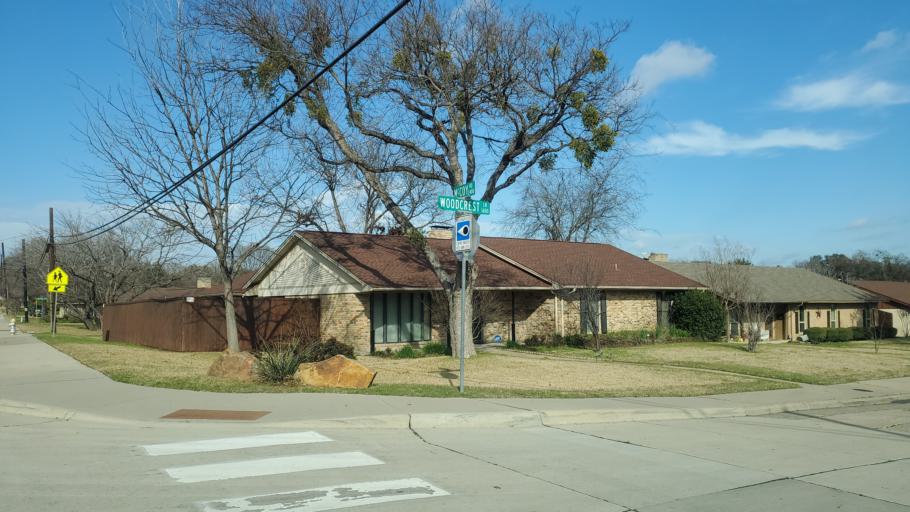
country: US
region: Texas
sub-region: Dallas County
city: Carrollton
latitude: 32.9812
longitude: -96.8975
